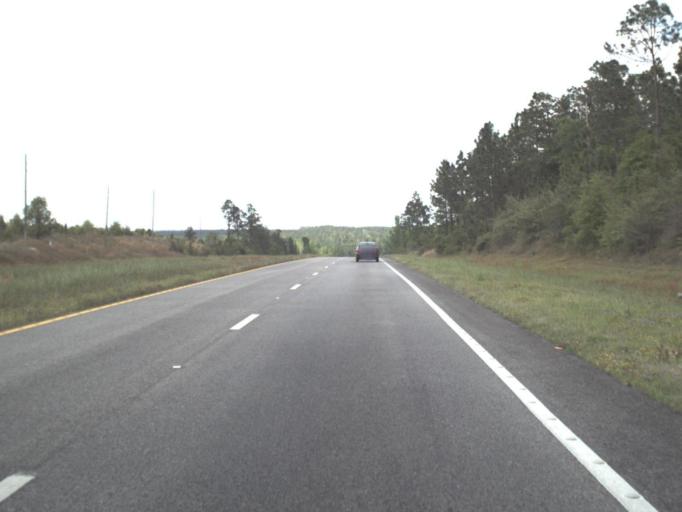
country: US
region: Florida
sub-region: Escambia County
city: Molino
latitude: 30.7657
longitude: -87.3409
